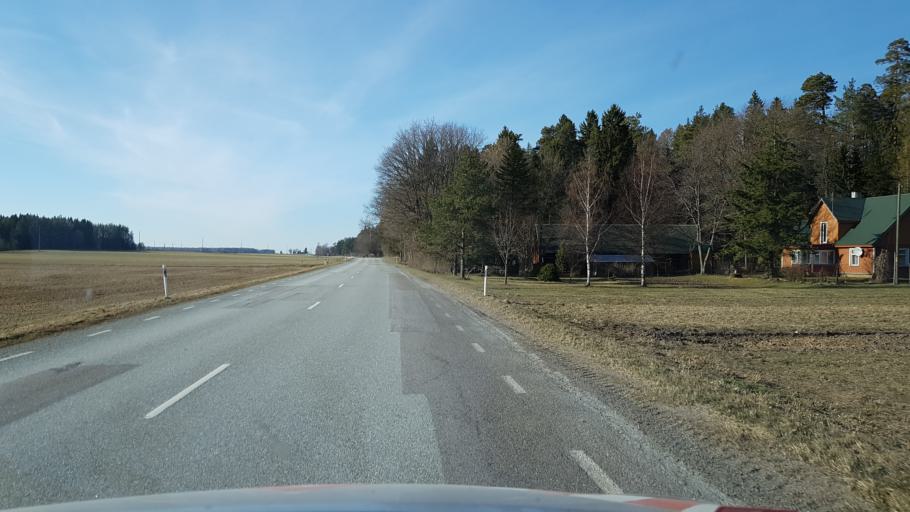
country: EE
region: Laeaene-Virumaa
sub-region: Vinni vald
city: Vinni
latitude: 59.1870
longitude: 26.5752
